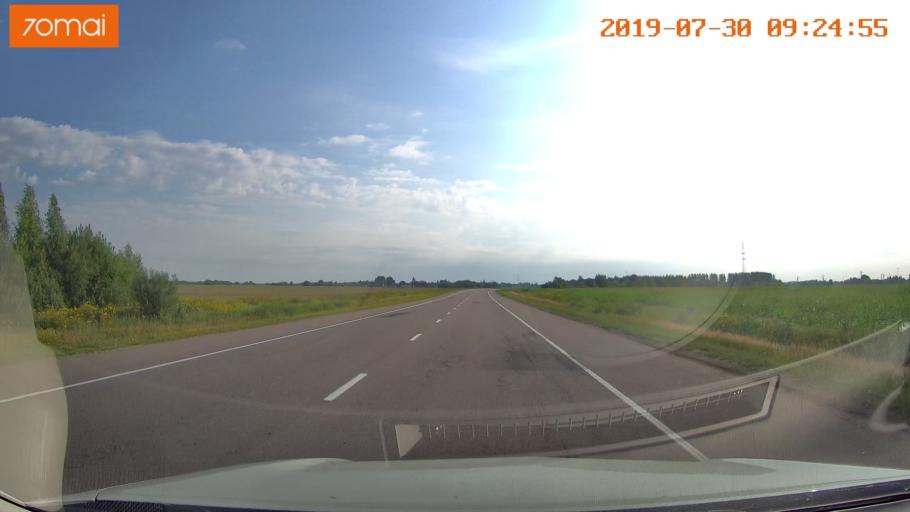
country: LT
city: Kybartai
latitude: 54.6357
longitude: 22.7041
